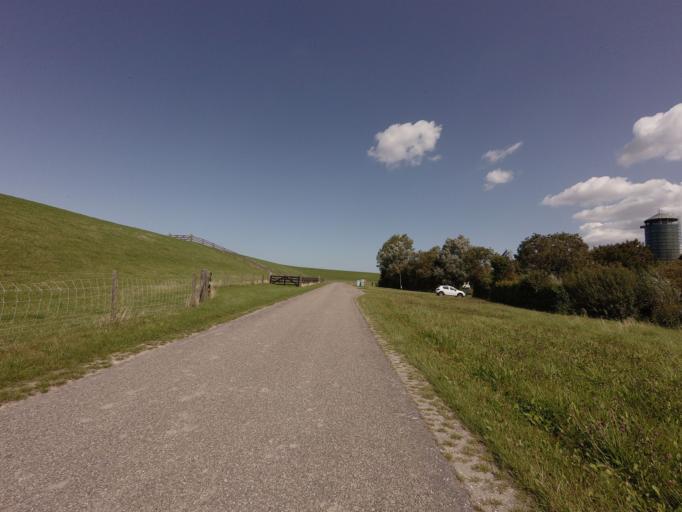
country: NL
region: Friesland
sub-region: Gemeente Ferwerderadiel
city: Hallum
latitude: 53.3282
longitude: 5.7710
